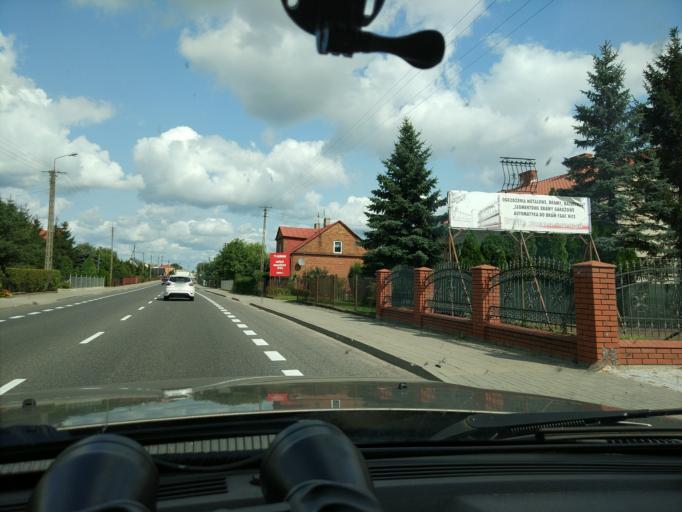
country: PL
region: Masovian Voivodeship
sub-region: Powiat mlawski
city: Wisniewo
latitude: 53.0612
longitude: 20.3472
